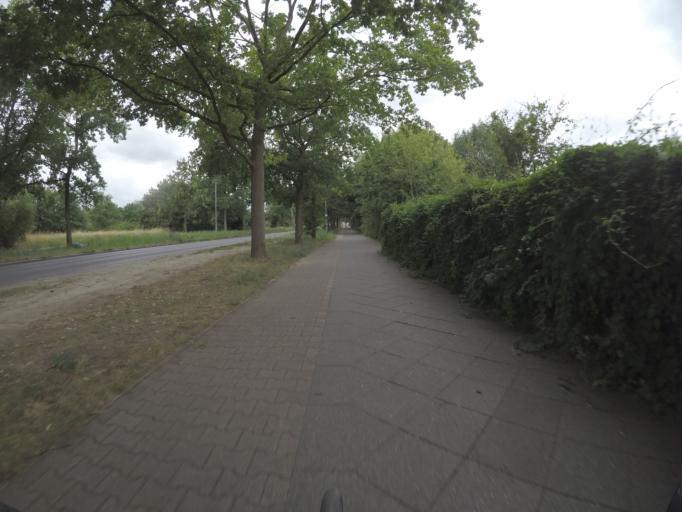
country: DE
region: Berlin
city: Mariendorf
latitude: 52.4394
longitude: 13.4072
